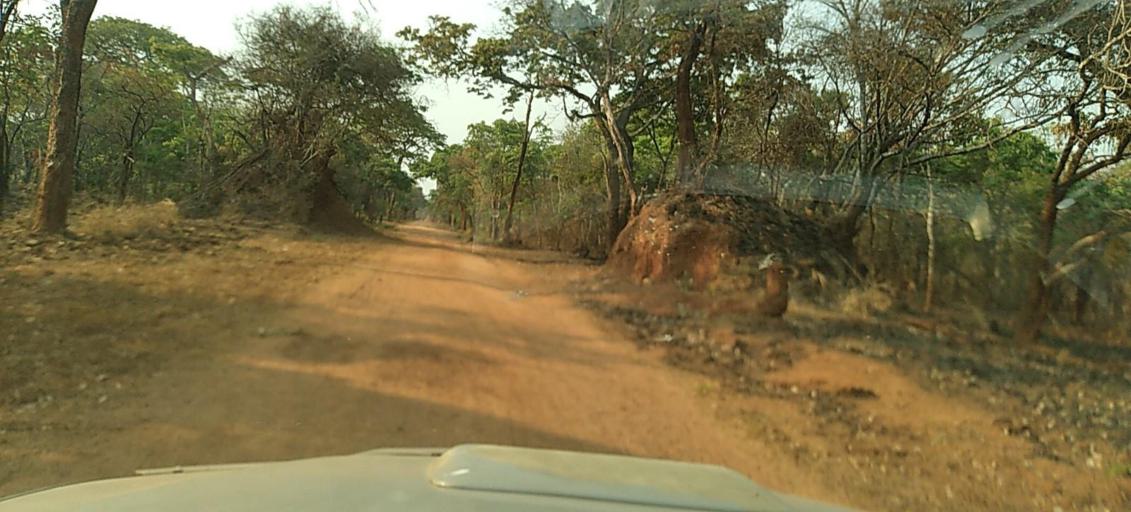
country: ZM
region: North-Western
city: Kasempa
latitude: -13.2902
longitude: 26.5553
